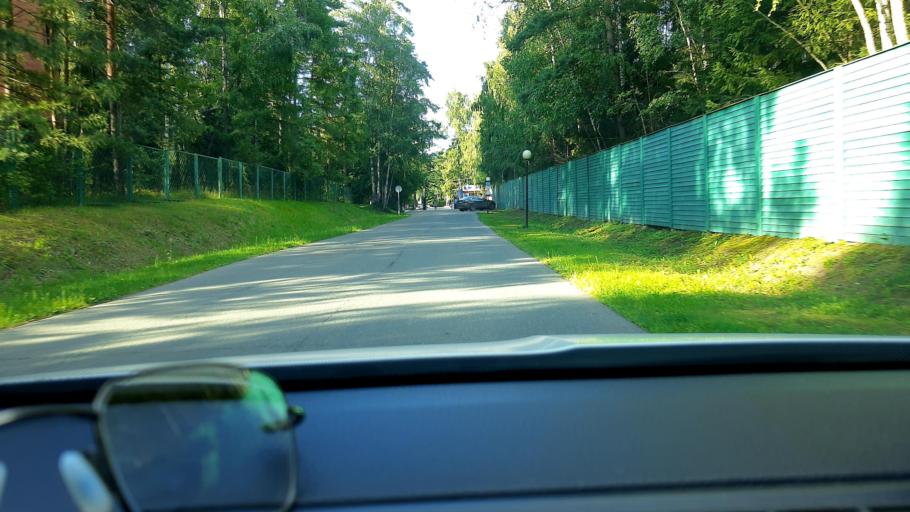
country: RU
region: Moskovskaya
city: Nikolina Gora
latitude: 55.7222
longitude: 36.9641
